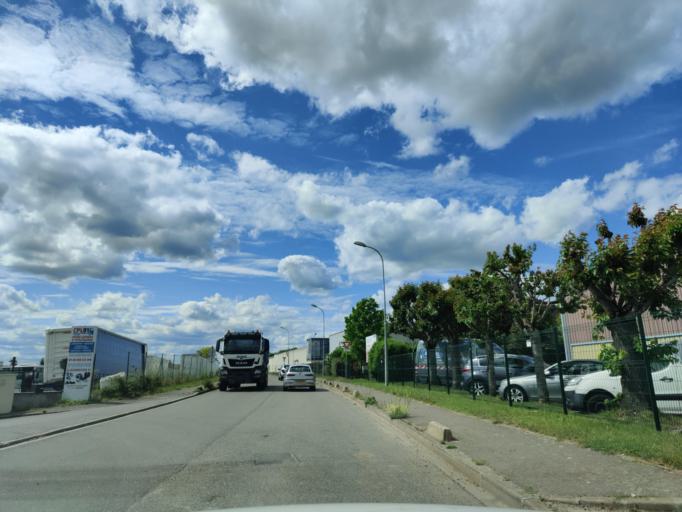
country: FR
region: Ile-de-France
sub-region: Departement de l'Essonne
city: Egly
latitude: 48.5736
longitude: 2.2060
